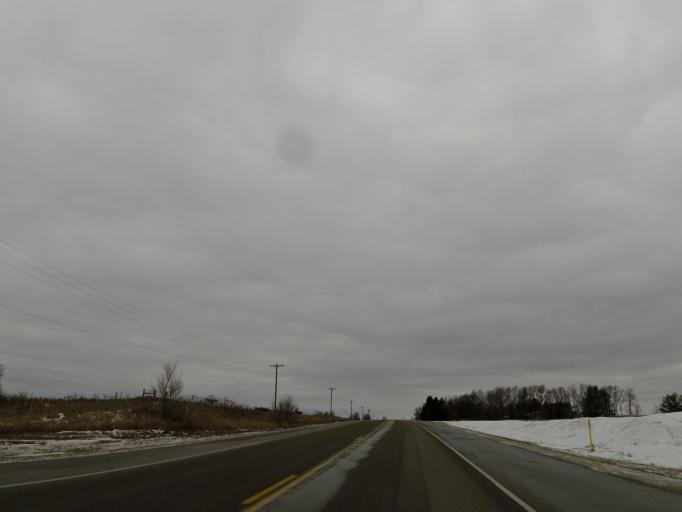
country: US
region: Minnesota
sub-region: Washington County
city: Cottage Grove
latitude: 44.8675
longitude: -92.9031
